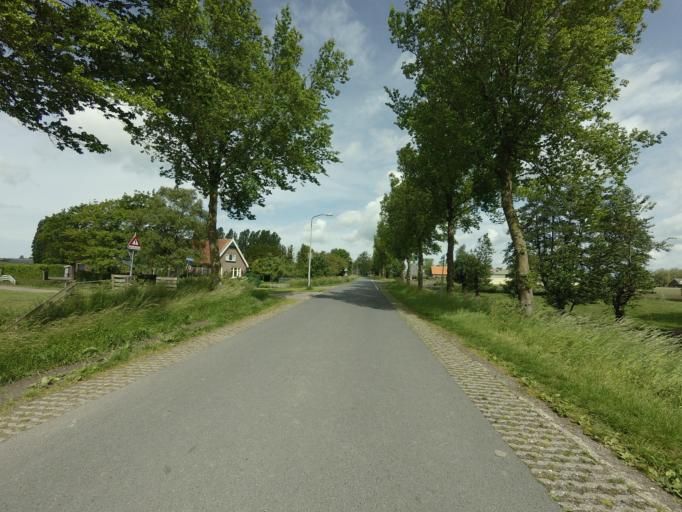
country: NL
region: North Holland
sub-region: Gemeente Hoorn
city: Hoorn
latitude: 52.6805
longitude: 5.0107
